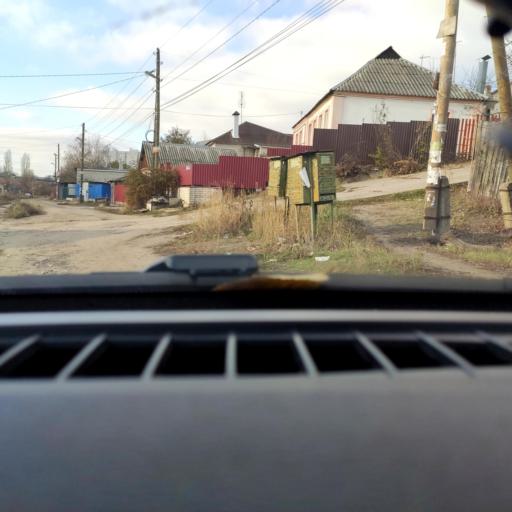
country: RU
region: Voronezj
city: Voronezh
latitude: 51.6717
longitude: 39.1451
